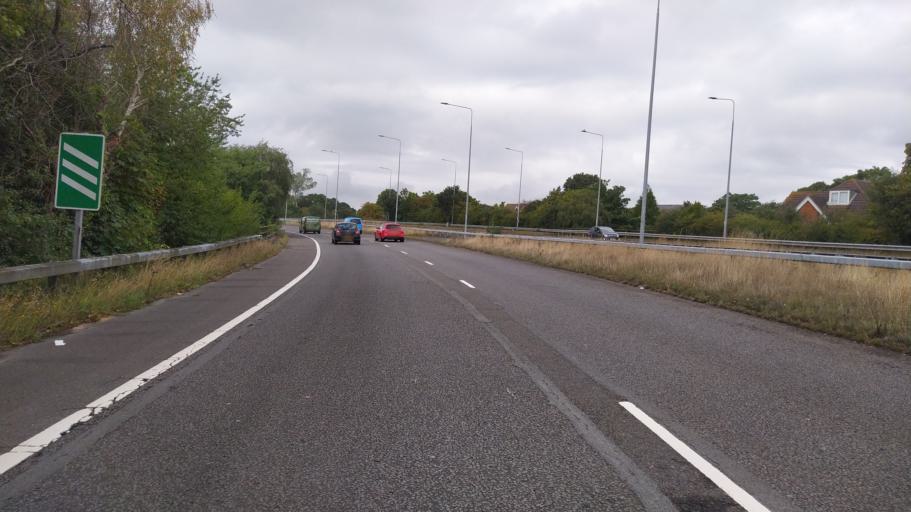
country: GB
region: England
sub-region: Bournemouth
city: Bournemouth
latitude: 50.7288
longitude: -1.8637
